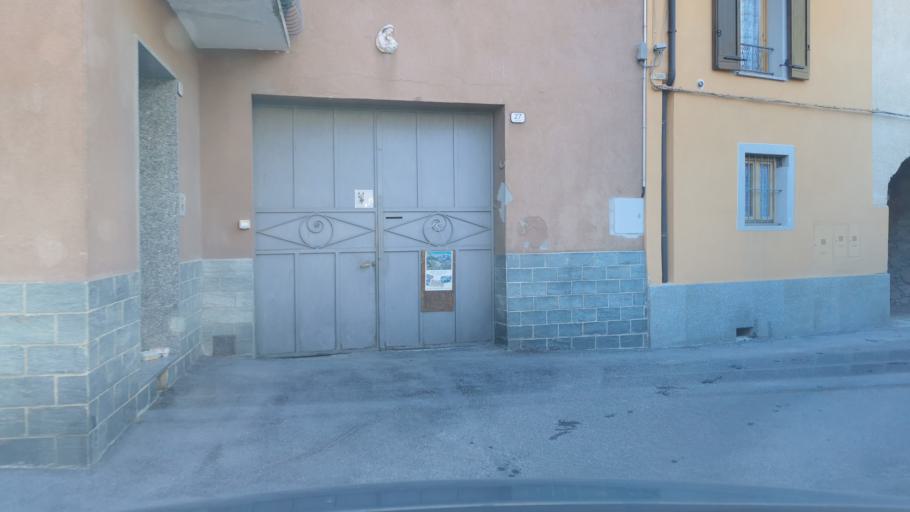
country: IT
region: Piedmont
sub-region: Provincia di Cuneo
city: Entracque
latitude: 44.2377
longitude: 7.3967
